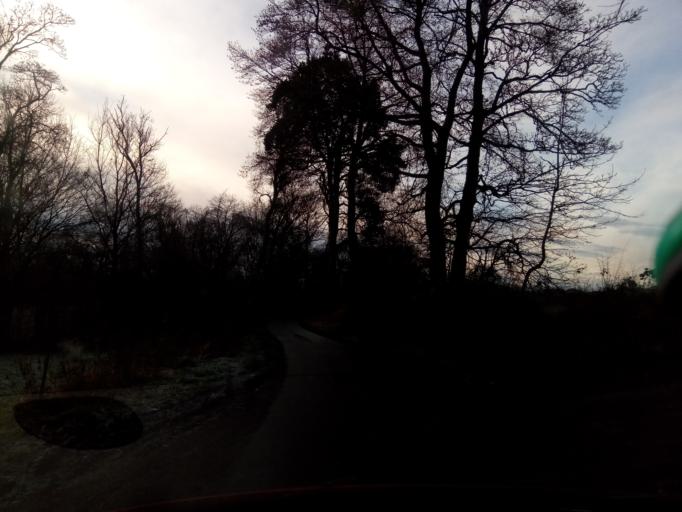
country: GB
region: Scotland
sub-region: The Scottish Borders
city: Hawick
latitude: 55.4539
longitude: -2.7297
